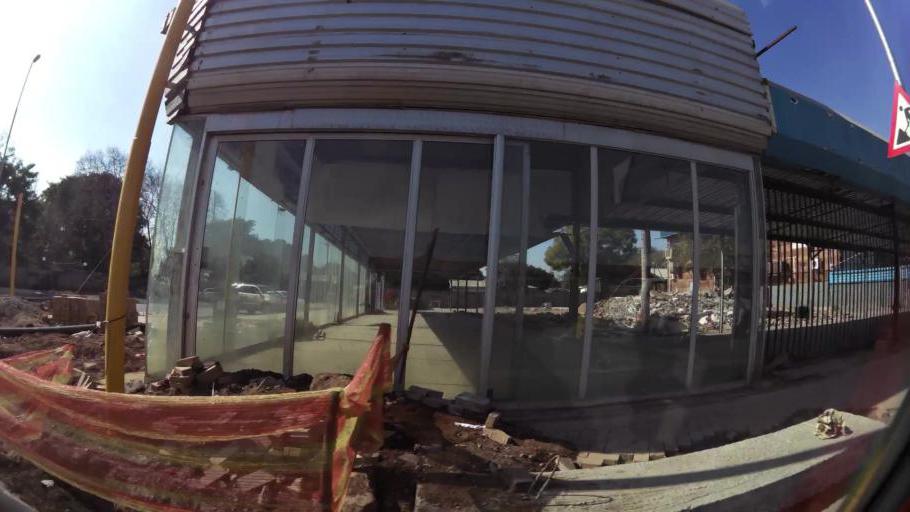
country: ZA
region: North-West
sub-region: Bojanala Platinum District Municipality
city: Rustenburg
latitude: -25.6629
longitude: 27.2405
